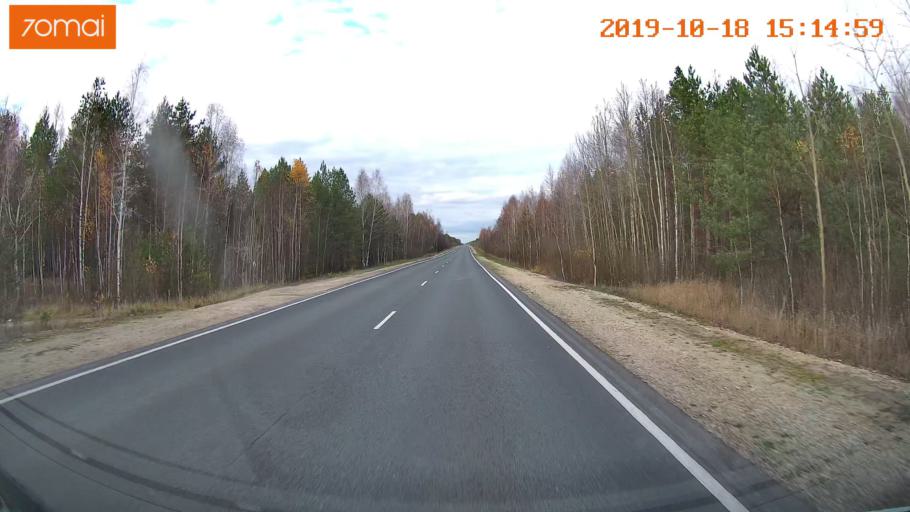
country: RU
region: Vladimir
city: Gus'-Khrustal'nyy
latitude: 55.6114
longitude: 40.7214
